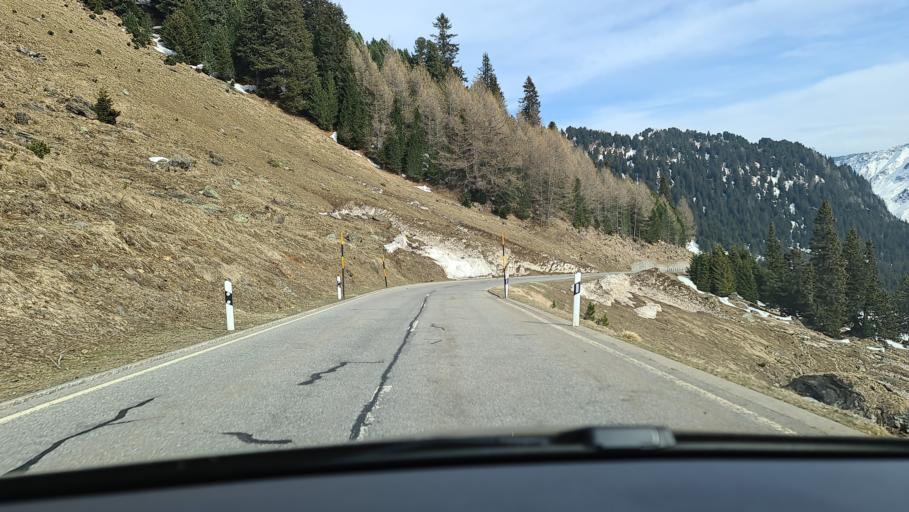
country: CH
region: Ticino
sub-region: Leventina District
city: Faido
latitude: 46.5369
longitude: 8.8376
